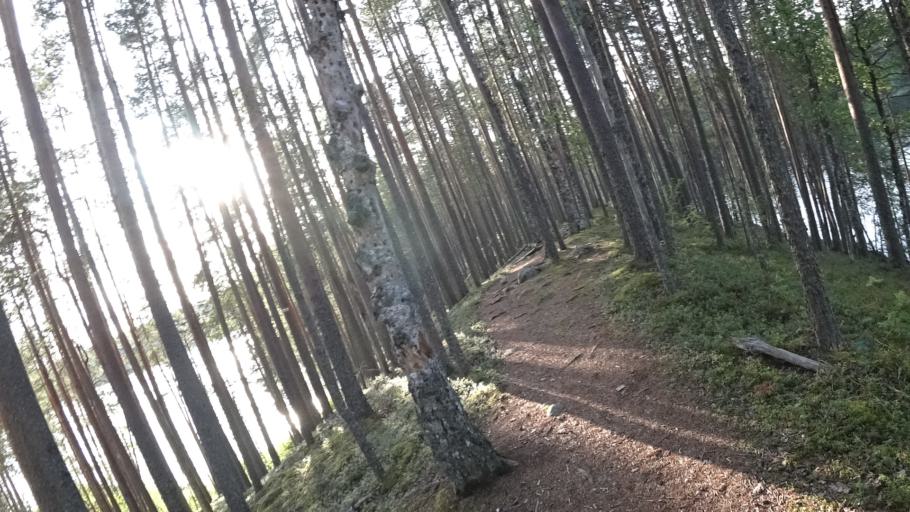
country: FI
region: North Karelia
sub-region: Joensuu
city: Ilomantsi
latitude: 62.5781
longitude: 31.1699
